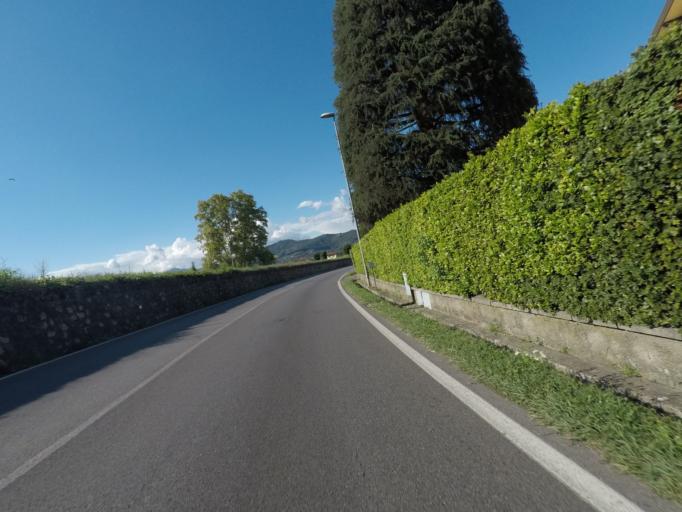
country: IT
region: Tuscany
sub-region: Provincia di Lucca
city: Lucca
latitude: 43.8685
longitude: 10.5075
